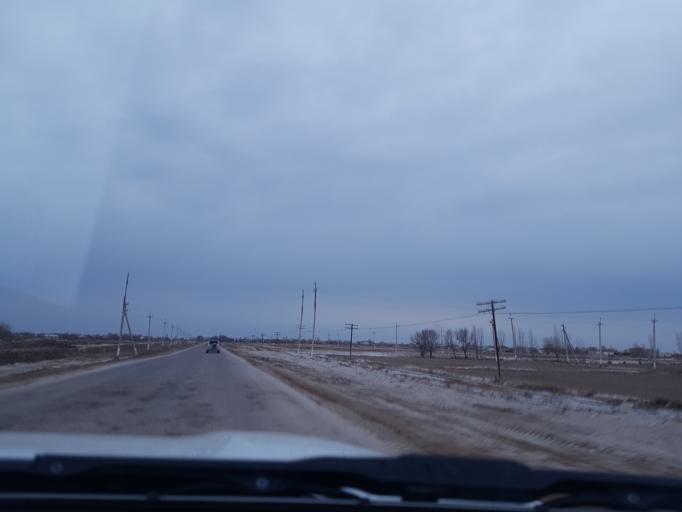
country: TM
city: Akdepe
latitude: 41.9670
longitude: 59.4945
